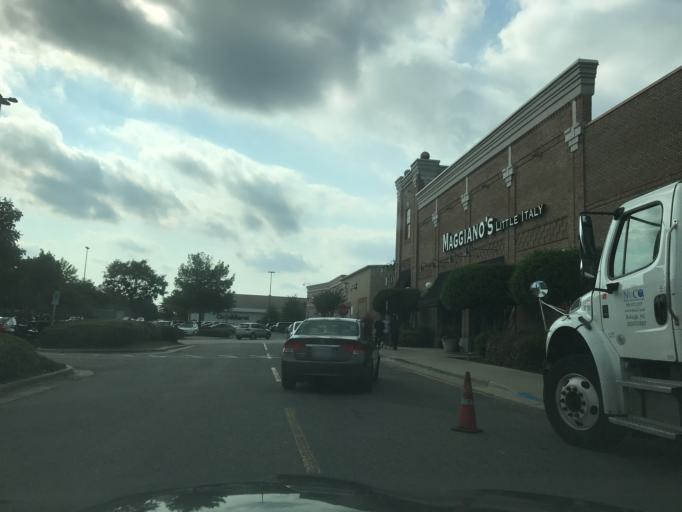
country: US
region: North Carolina
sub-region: Durham County
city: Durham
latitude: 35.9044
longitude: -78.9439
